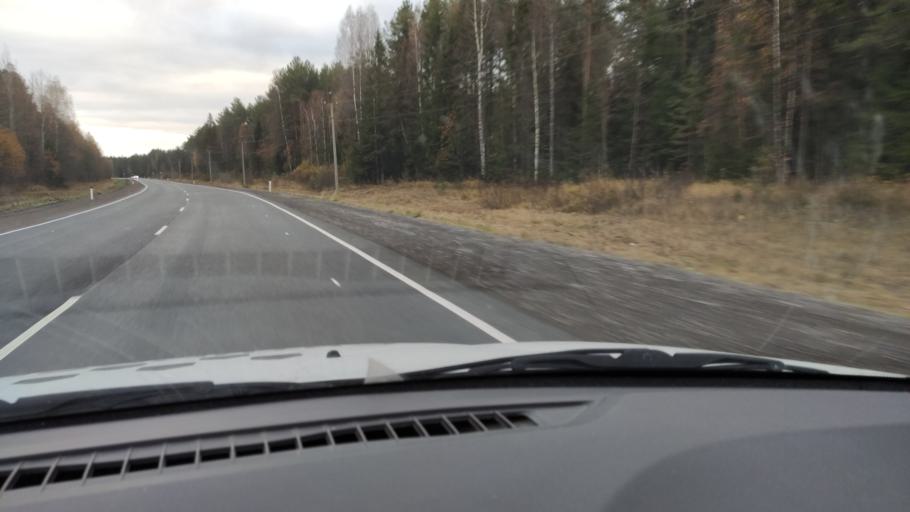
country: RU
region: Kirov
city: Belaya Kholunitsa
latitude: 58.8448
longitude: 50.7658
